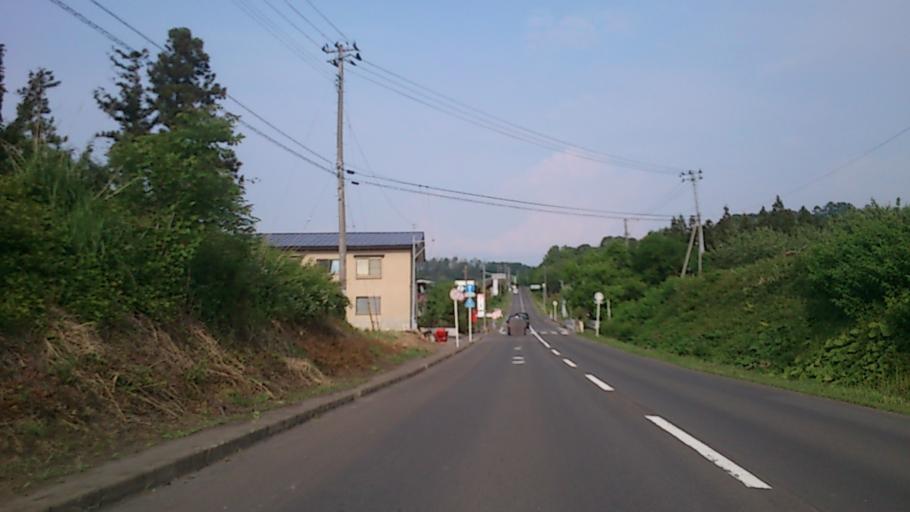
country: JP
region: Aomori
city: Hirosaki
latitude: 40.5620
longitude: 140.4420
